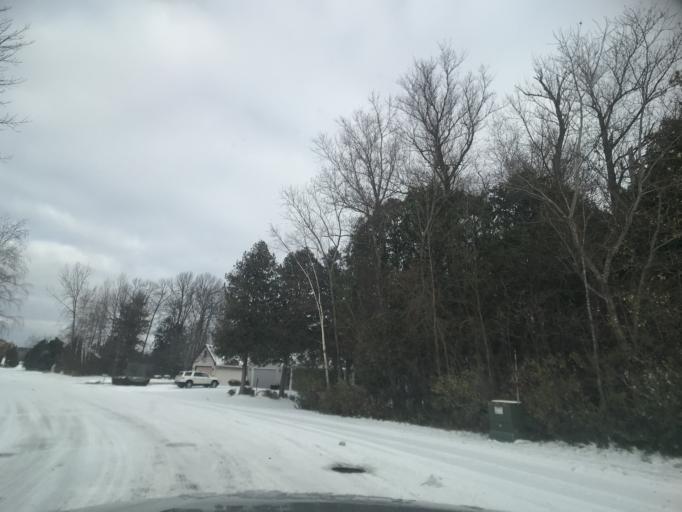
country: US
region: Wisconsin
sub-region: Door County
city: Sturgeon Bay
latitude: 44.8199
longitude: -87.3712
